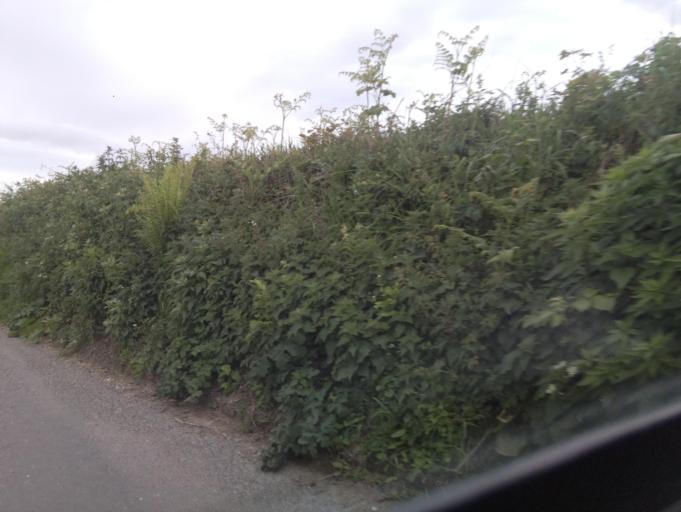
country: GB
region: England
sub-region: Devon
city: Dartmouth
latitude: 50.3275
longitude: -3.6421
